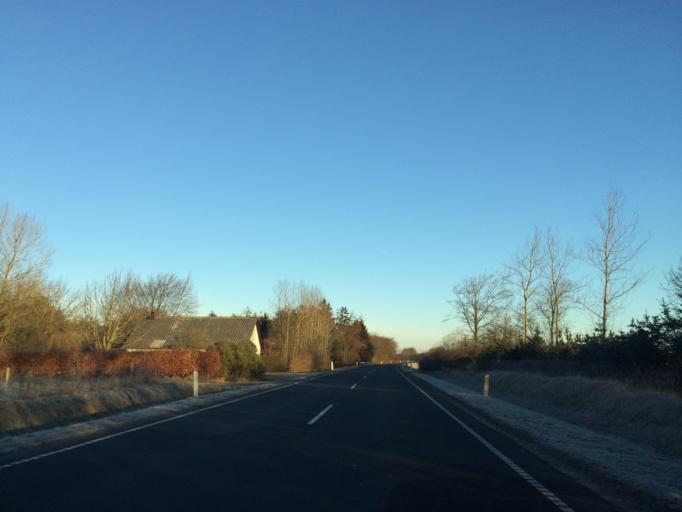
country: DK
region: Central Jutland
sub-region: Holstebro Kommune
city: Ulfborg
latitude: 56.3516
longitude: 8.3395
